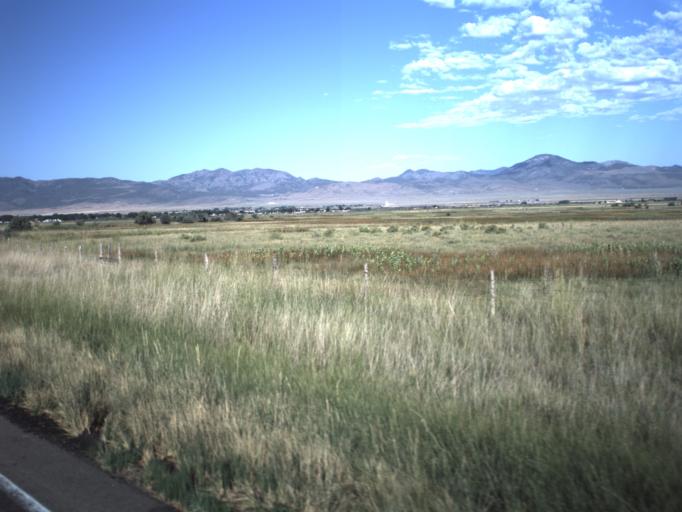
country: US
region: Utah
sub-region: Utah County
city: Genola
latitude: 39.9612
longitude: -111.8653
